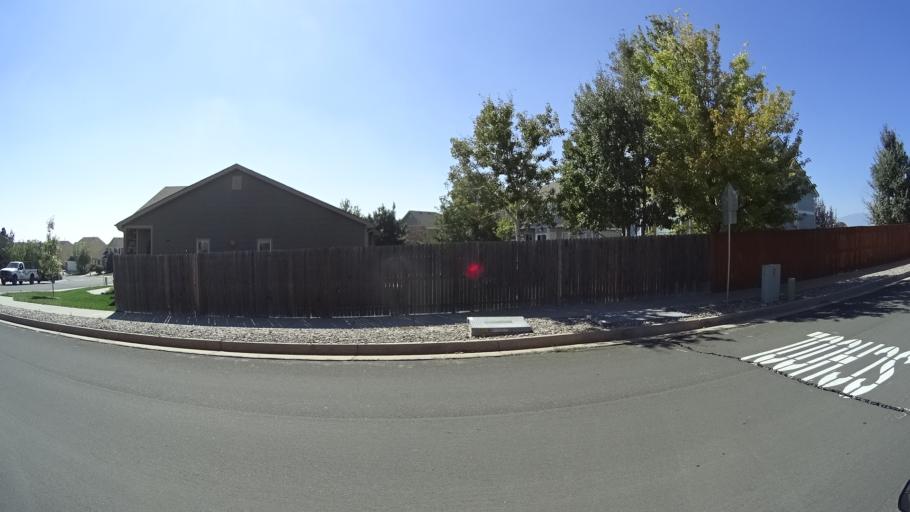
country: US
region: Colorado
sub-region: El Paso County
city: Cimarron Hills
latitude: 38.8958
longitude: -104.6961
